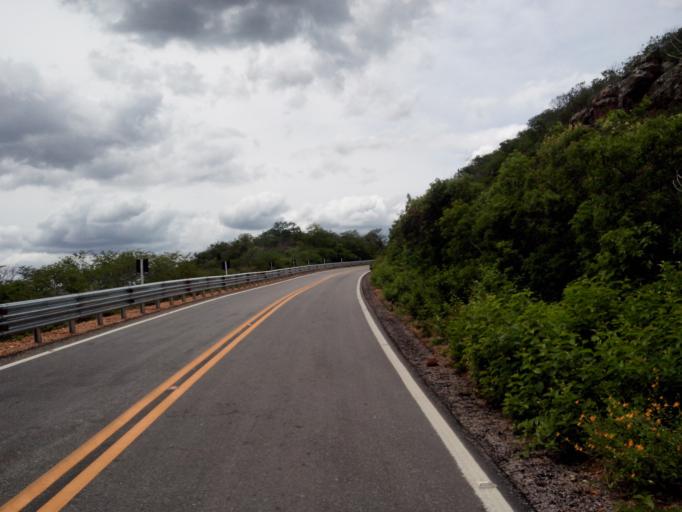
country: BR
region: Piaui
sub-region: Sao Raimundo Nonato
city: Sao Raimundo Nonato
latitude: -8.7898
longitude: -42.4803
